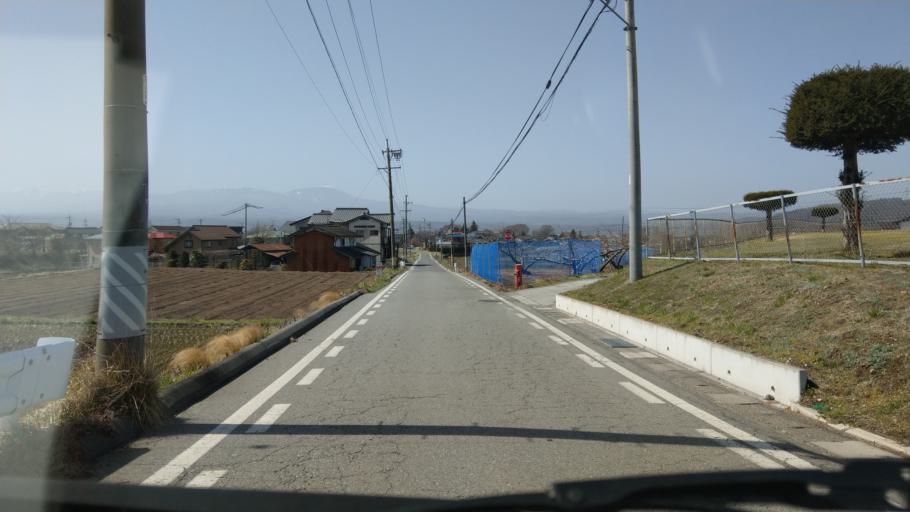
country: JP
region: Nagano
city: Komoro
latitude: 36.3020
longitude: 138.4464
